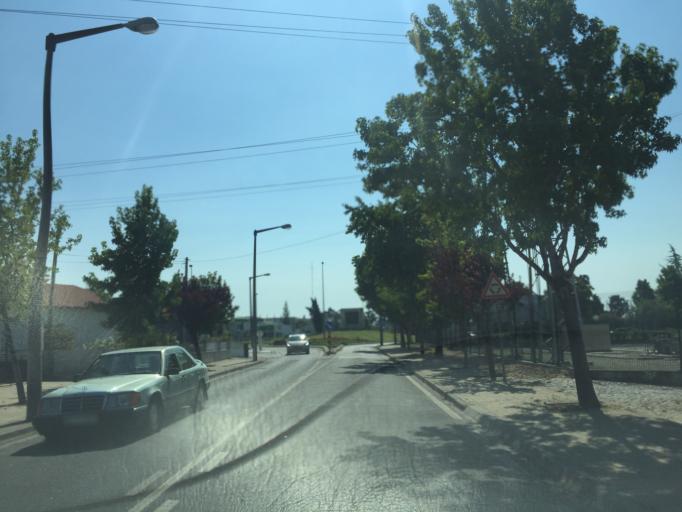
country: PT
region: Coimbra
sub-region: Cantanhede
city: Cantanhede
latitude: 40.3492
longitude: -8.5834
